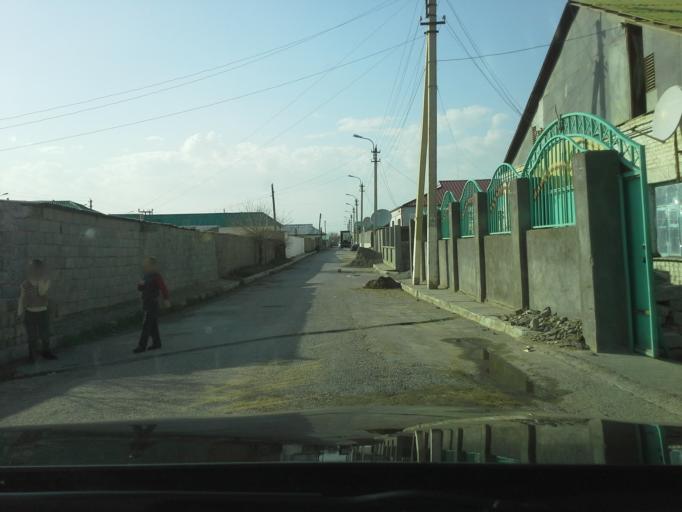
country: TM
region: Ahal
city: Abadan
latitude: 38.0175
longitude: 58.2366
